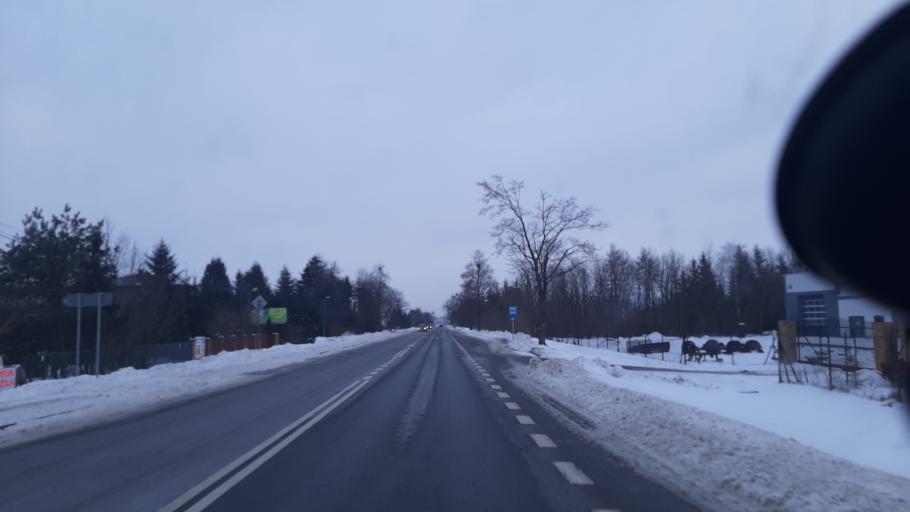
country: PL
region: Lublin Voivodeship
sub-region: Powiat pulawski
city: Markuszow
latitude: 51.3774
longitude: 22.2464
